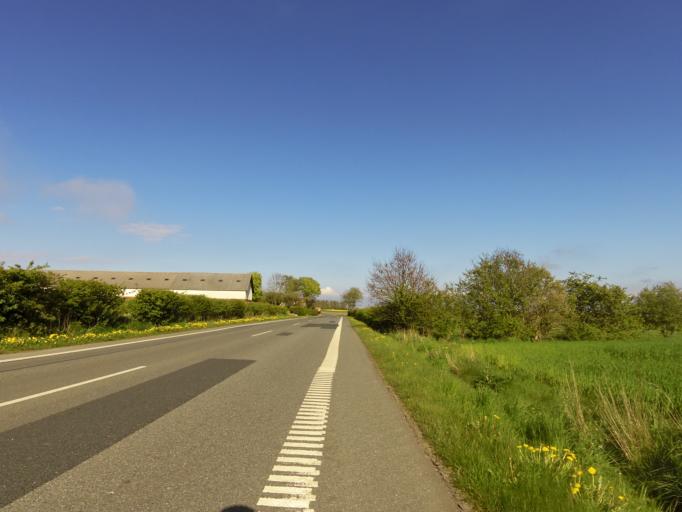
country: DK
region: South Denmark
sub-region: Tonder Kommune
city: Sherrebek
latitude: 55.1548
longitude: 8.8032
